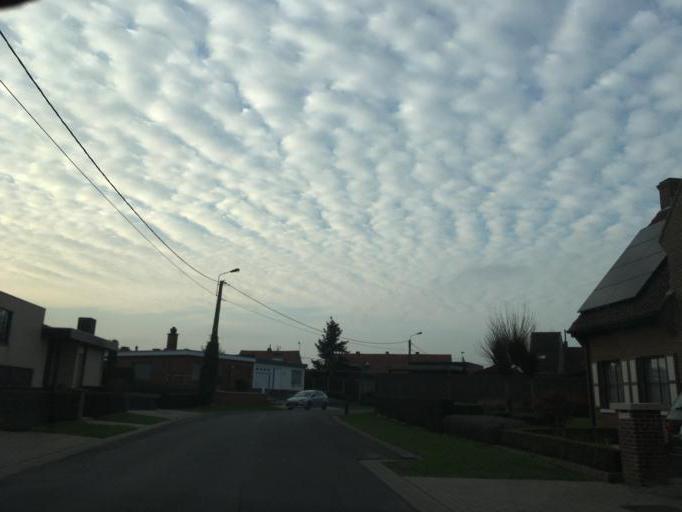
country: BE
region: Flanders
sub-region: Provincie West-Vlaanderen
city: Roeselare
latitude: 50.9317
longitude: 3.1243
